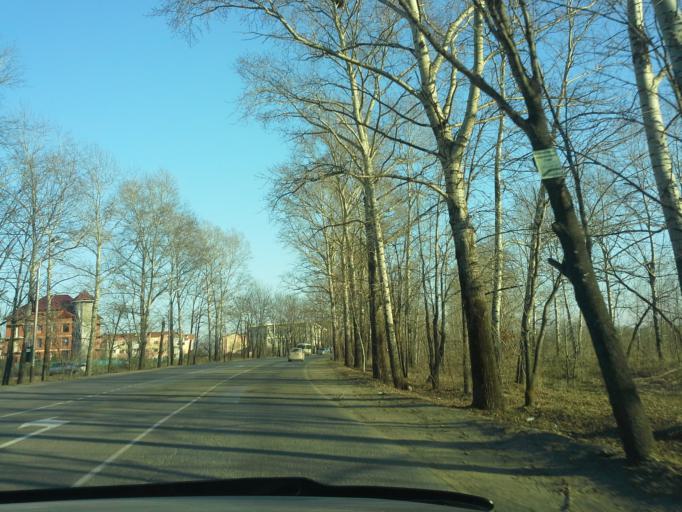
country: RU
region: Khabarovsk Krai
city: Topolevo
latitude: 48.4786
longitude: 135.1585
